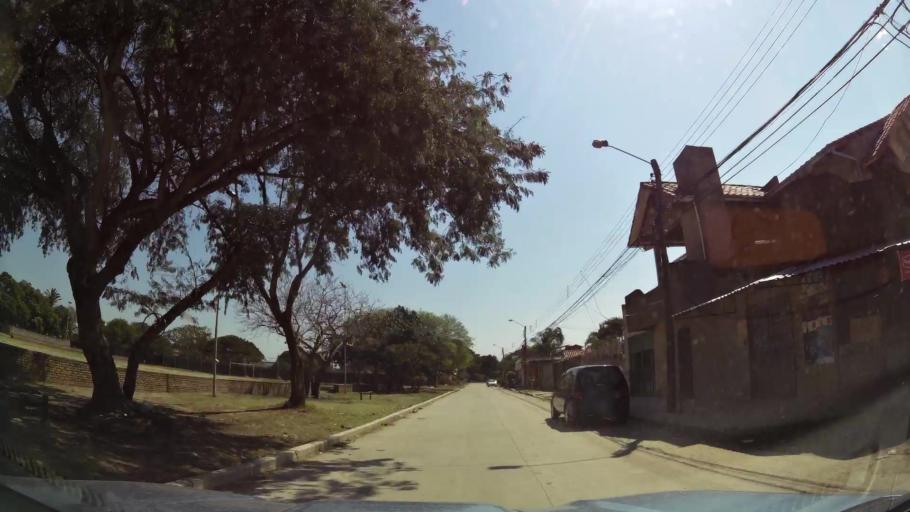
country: BO
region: Santa Cruz
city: Santa Cruz de la Sierra
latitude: -17.7405
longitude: -63.1552
